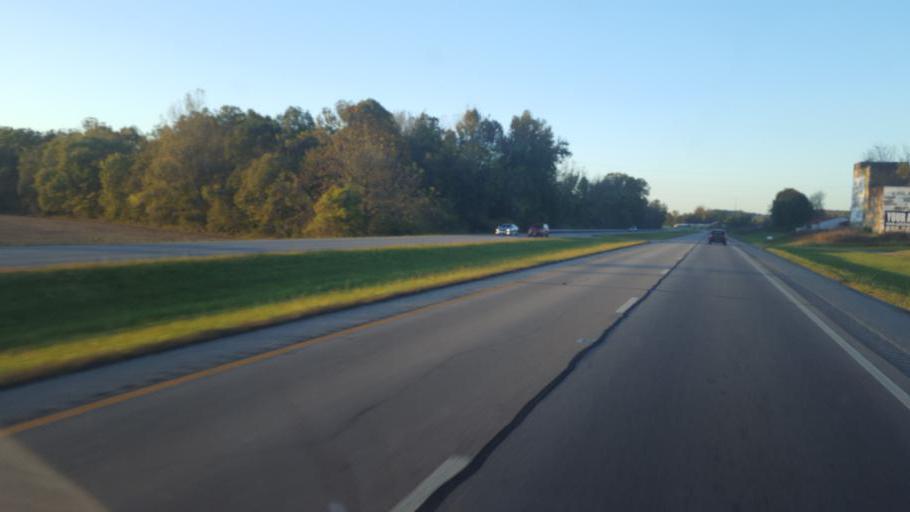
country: US
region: Ohio
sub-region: Pike County
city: Piketon
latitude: 38.9868
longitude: -83.0231
